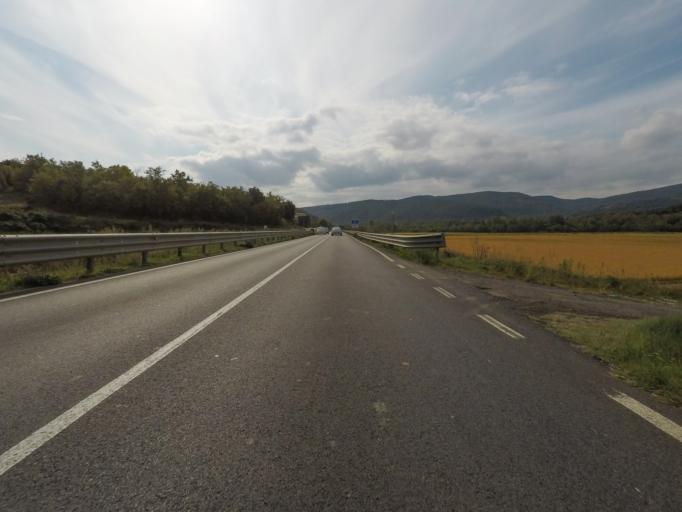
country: IT
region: Tuscany
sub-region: Provincia di Siena
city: Murlo
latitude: 43.1567
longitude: 11.2907
